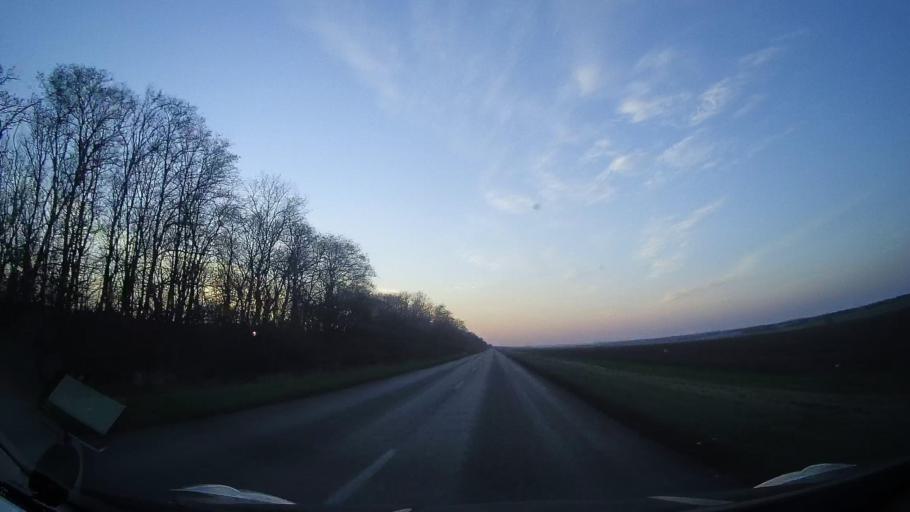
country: RU
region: Rostov
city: Zernograd
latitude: 46.9655
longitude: 40.3815
